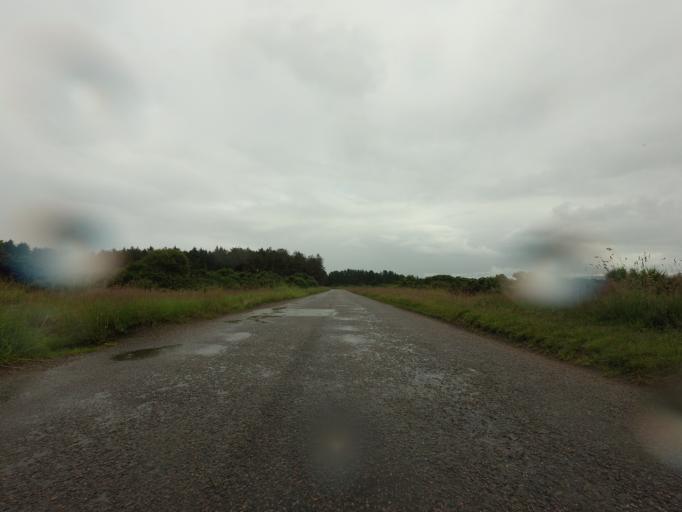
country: GB
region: Scotland
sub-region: Moray
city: Fochabers
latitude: 57.6589
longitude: -3.0715
